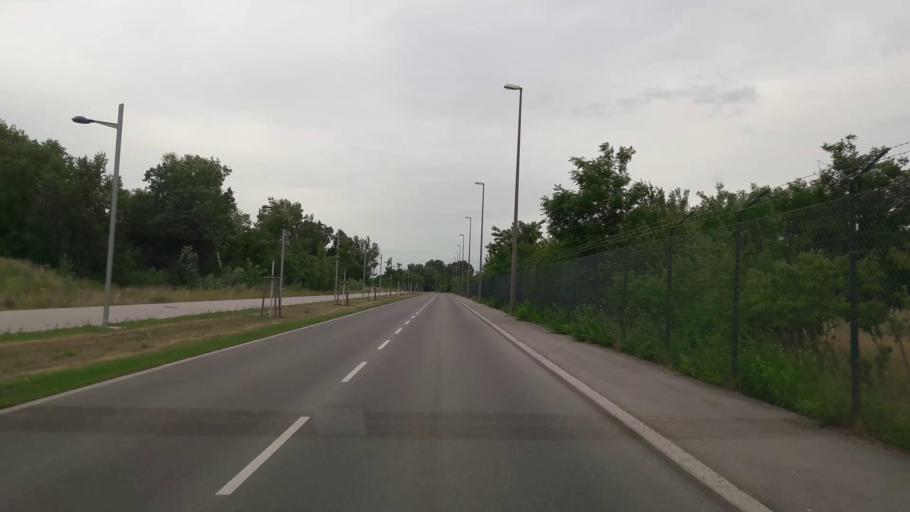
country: AT
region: Lower Austria
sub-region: Politischer Bezirk Ganserndorf
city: Gross-Enzersdorf
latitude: 48.2196
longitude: 16.5118
